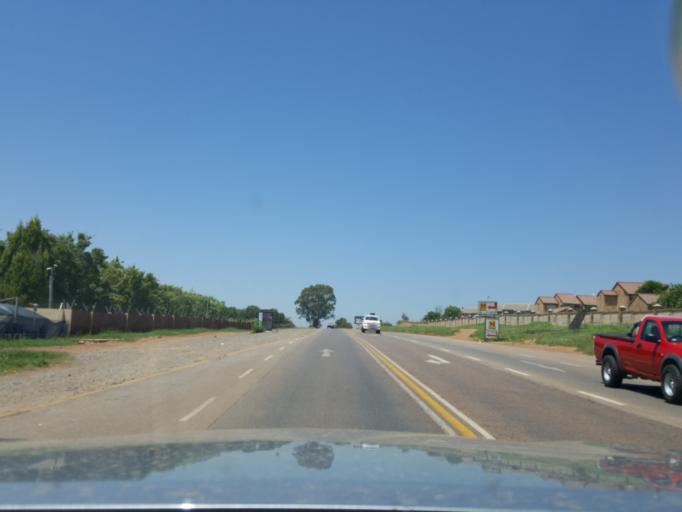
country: ZA
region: Gauteng
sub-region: City of Tshwane Metropolitan Municipality
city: Centurion
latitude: -25.8415
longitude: 28.3257
